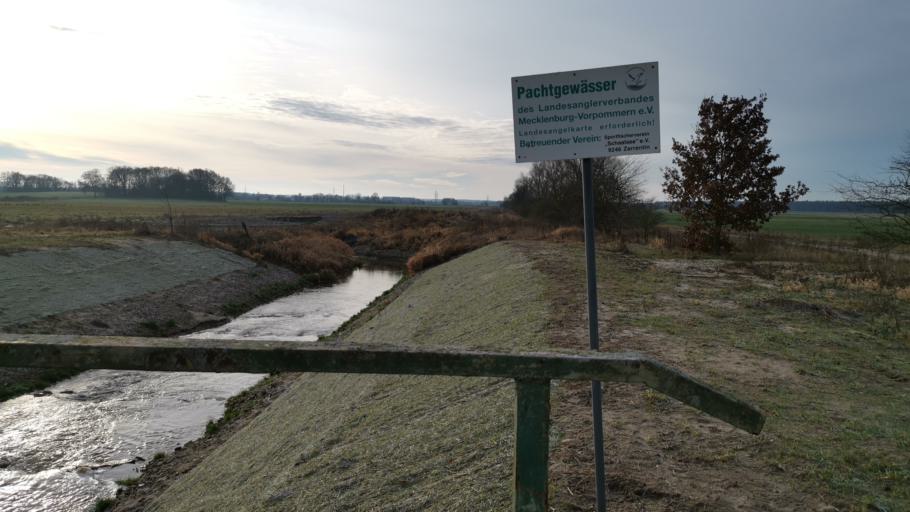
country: DE
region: Schleswig-Holstein
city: Hollenbek
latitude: 53.5426
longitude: 10.8369
